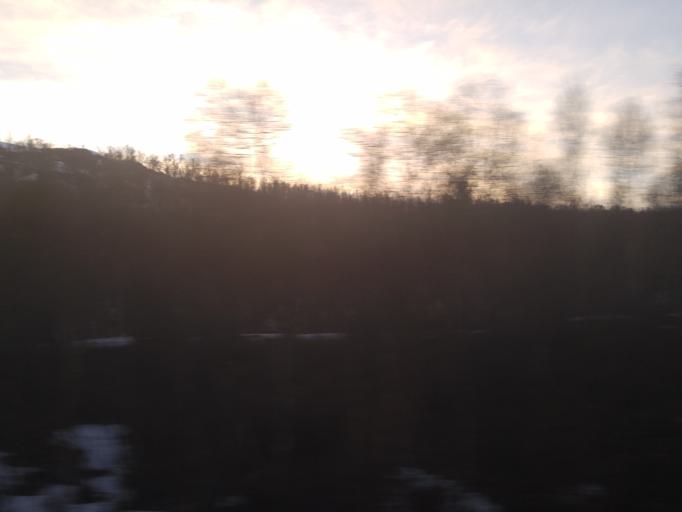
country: NO
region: Sor-Trondelag
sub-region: Oppdal
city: Oppdal
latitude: 62.2985
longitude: 9.5942
